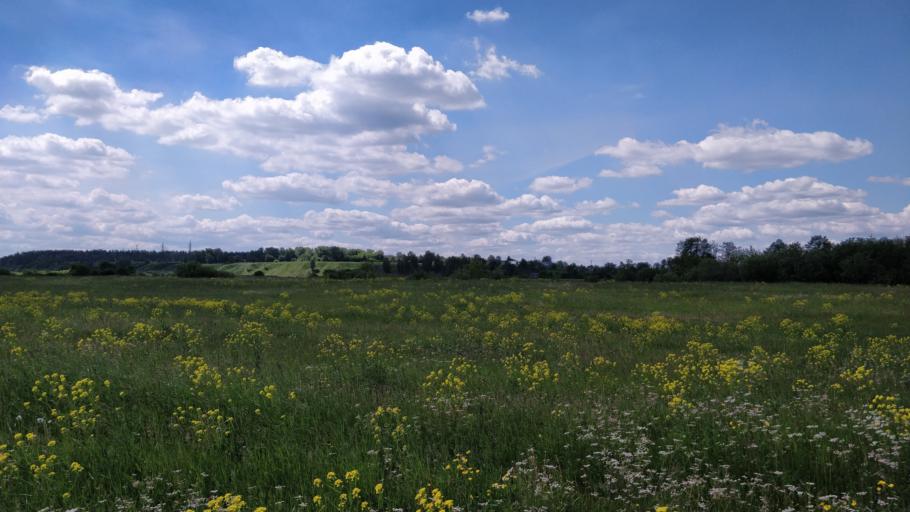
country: RU
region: Perm
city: Kungur
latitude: 57.4664
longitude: 56.9285
